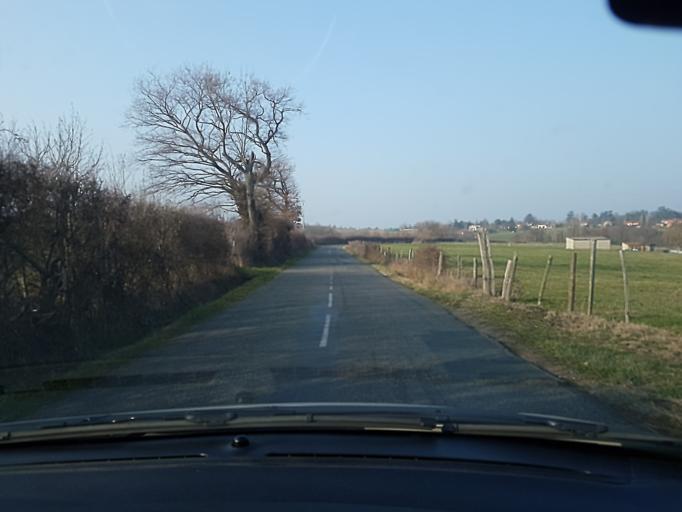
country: FR
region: Rhone-Alpes
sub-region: Departement du Rhone
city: Orlienas
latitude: 45.6478
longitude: 4.7130
